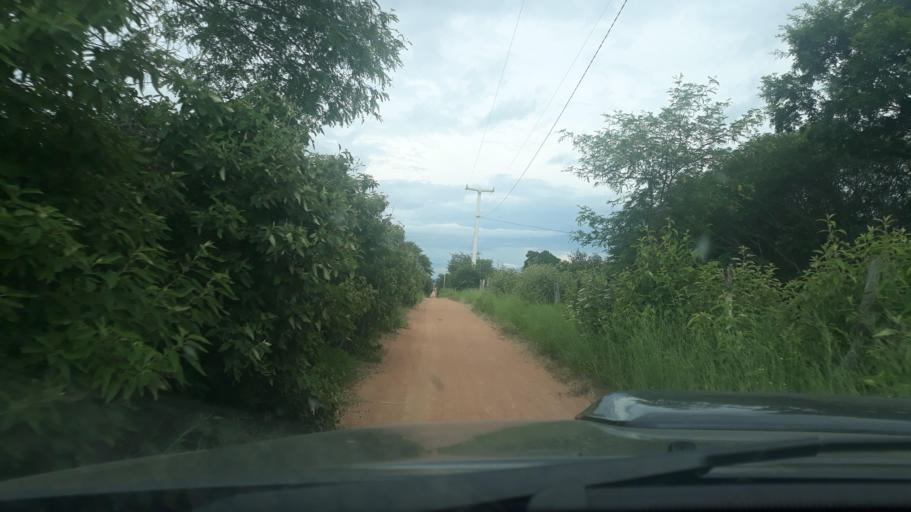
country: BR
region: Bahia
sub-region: Riacho De Santana
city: Riacho de Santana
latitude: -13.8618
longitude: -43.0283
